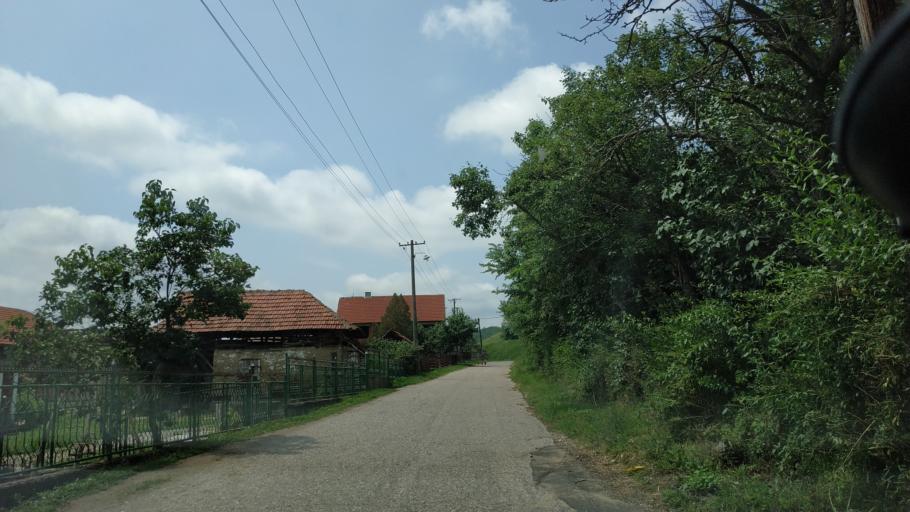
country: RS
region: Central Serbia
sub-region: Nisavski Okrug
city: Aleksinac
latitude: 43.4267
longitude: 21.7416
